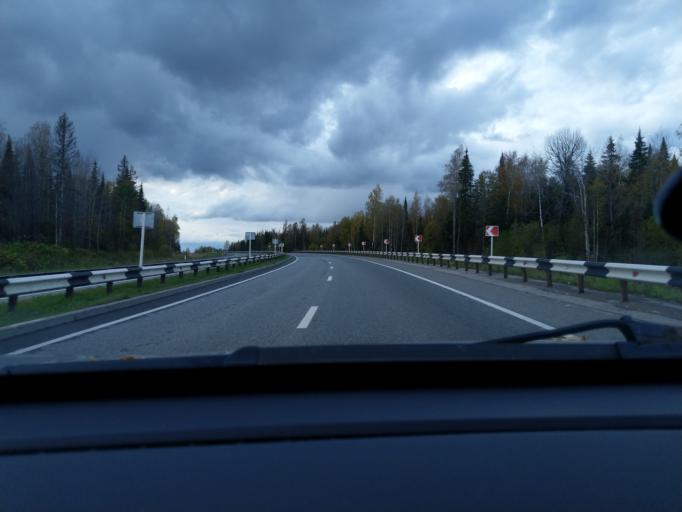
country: RU
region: Perm
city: Polazna
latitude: 58.3378
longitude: 56.4771
